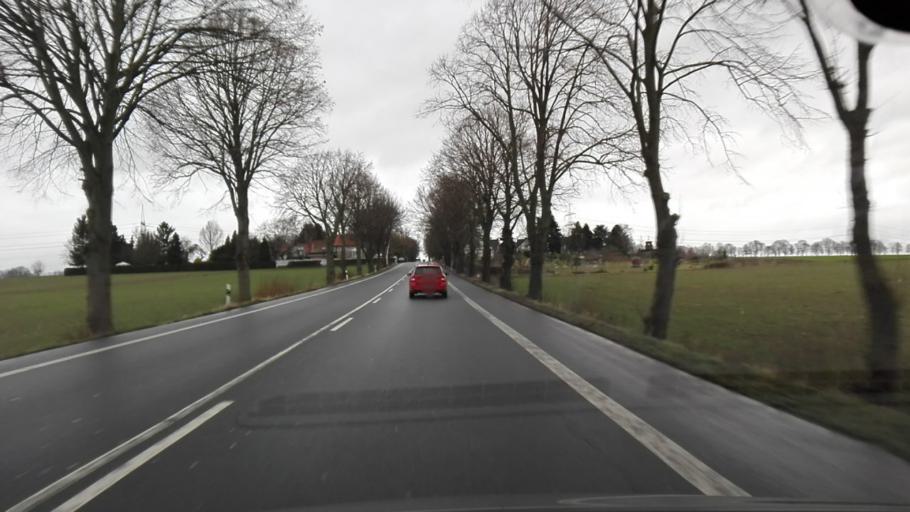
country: DE
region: North Rhine-Westphalia
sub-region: Regierungsbezirk Arnsberg
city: Unna
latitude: 51.4939
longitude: 7.7054
